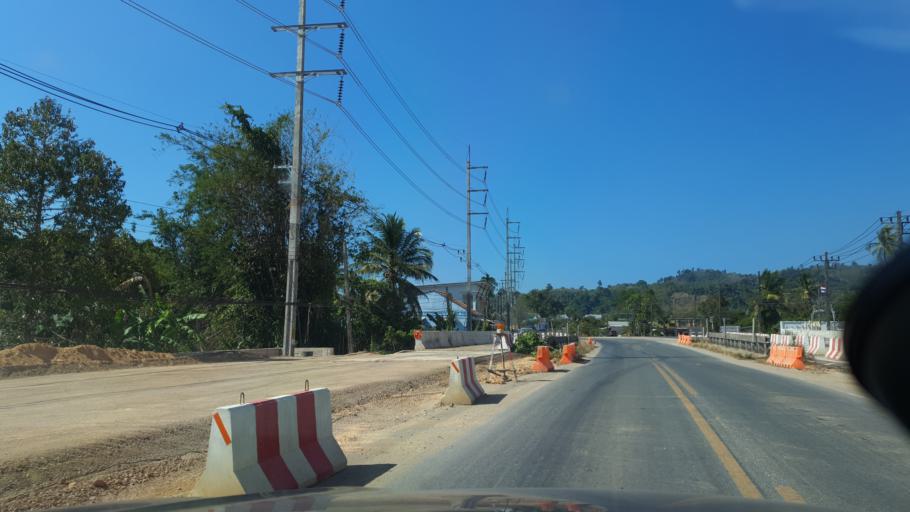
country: TH
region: Phangnga
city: Ban Khao Lak
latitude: 8.5987
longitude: 98.2551
